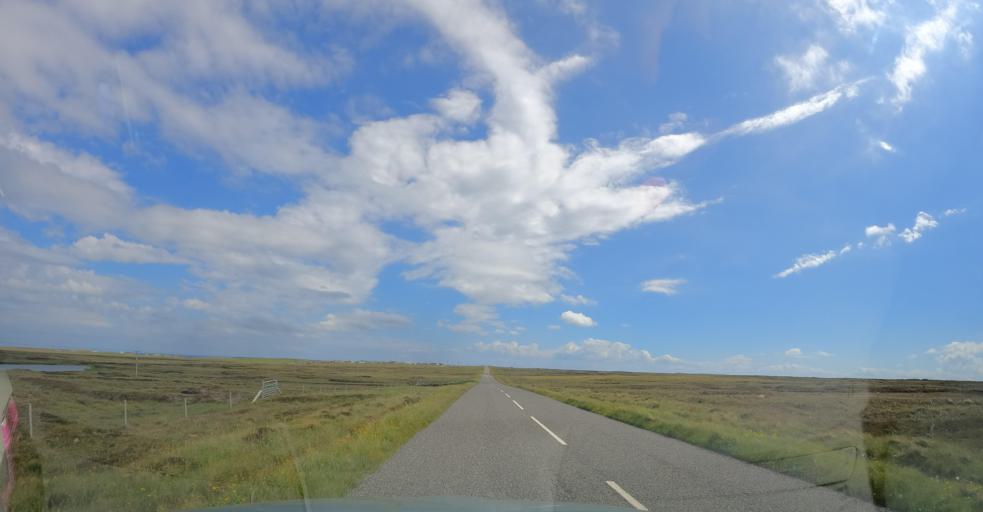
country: GB
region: Scotland
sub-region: Eilean Siar
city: Isle of Lewis
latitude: 58.4603
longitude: -6.3302
